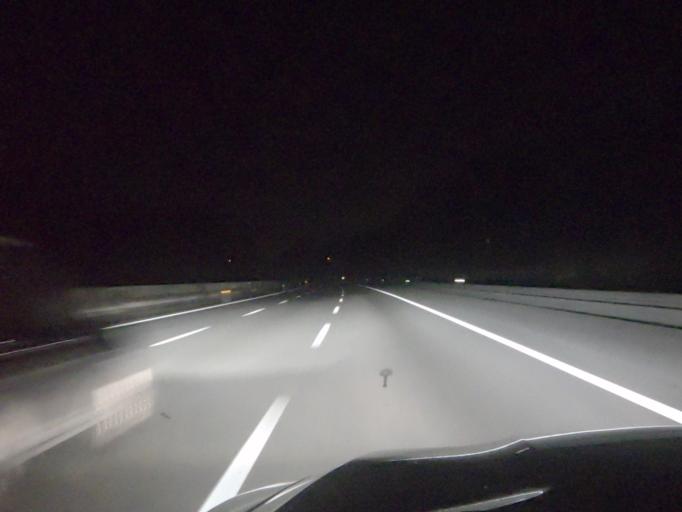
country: PT
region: Aveiro
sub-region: Estarreja
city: Avanca
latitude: 40.8141
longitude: -8.5485
